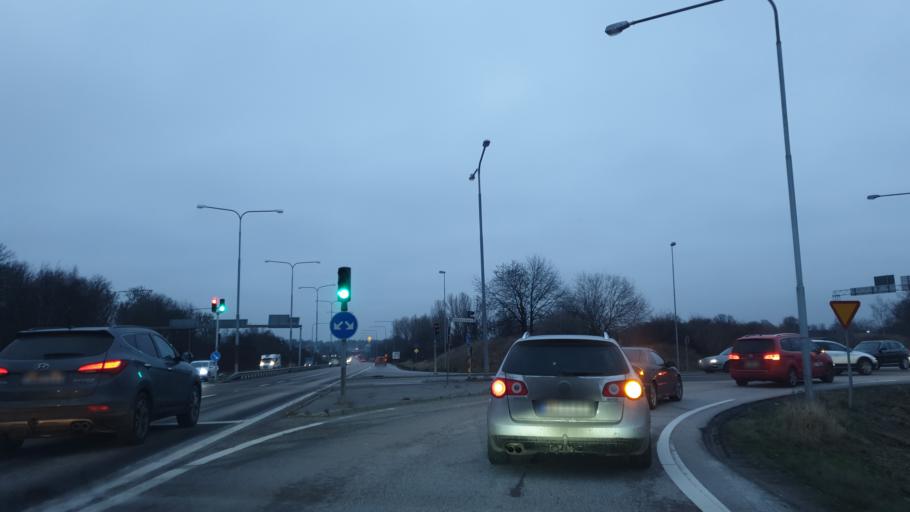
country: SE
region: Blekinge
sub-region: Karlskrona Kommun
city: Karlskrona
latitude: 56.1961
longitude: 15.6319
